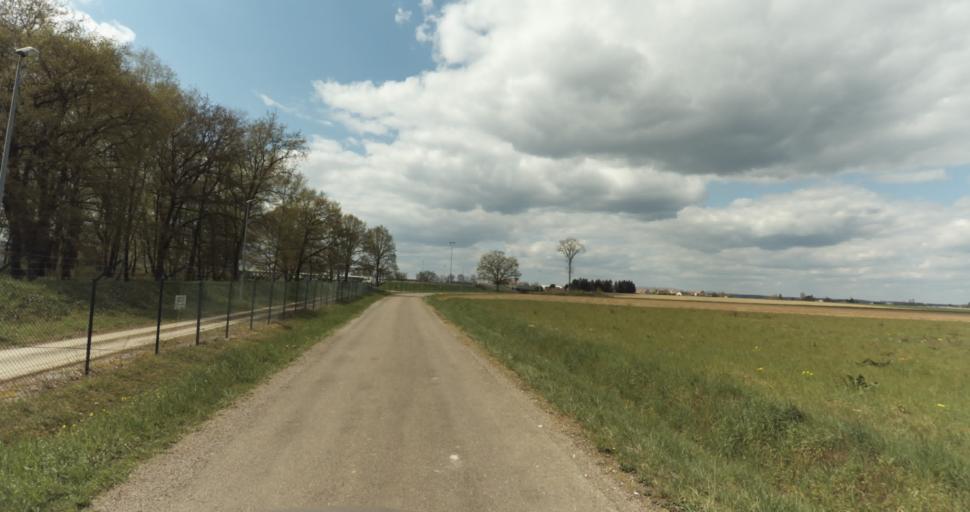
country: FR
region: Bourgogne
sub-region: Departement de la Cote-d'Or
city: Auxonne
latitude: 47.1755
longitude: 5.4120
